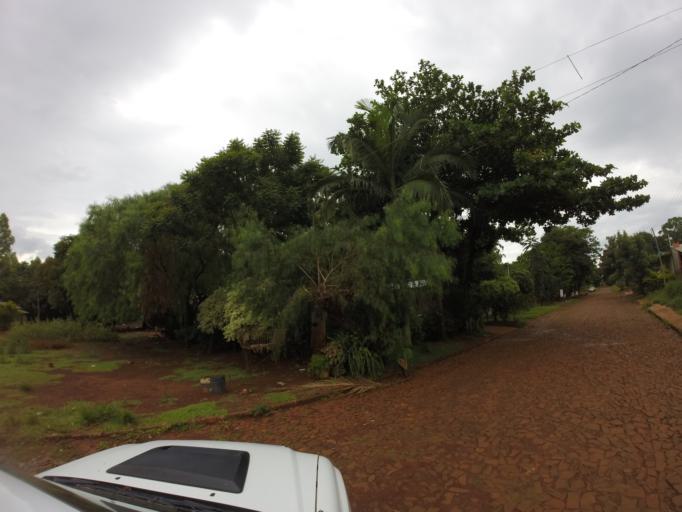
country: PY
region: Alto Parana
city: Ciudad del Este
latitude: -25.4158
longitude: -54.6532
